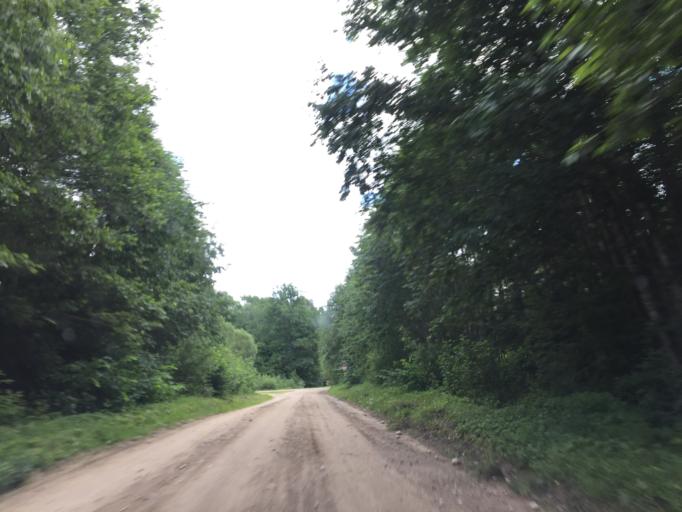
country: LV
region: Malpils
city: Malpils
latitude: 56.8866
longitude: 24.9807
